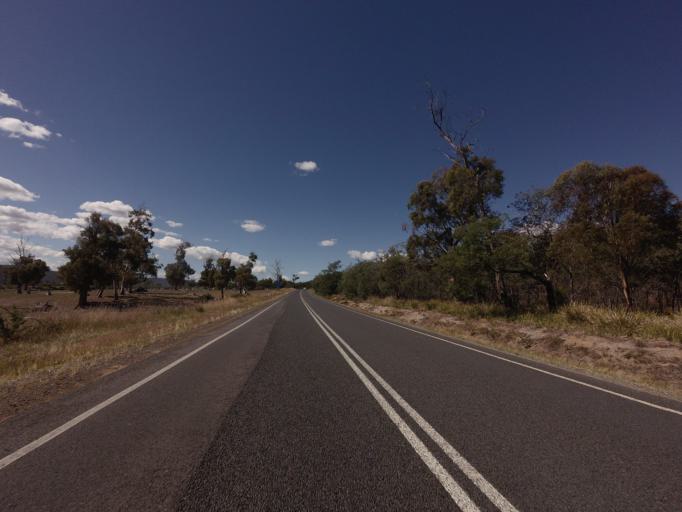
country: AU
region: Tasmania
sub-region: Break O'Day
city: St Helens
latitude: -41.6838
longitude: 147.8843
